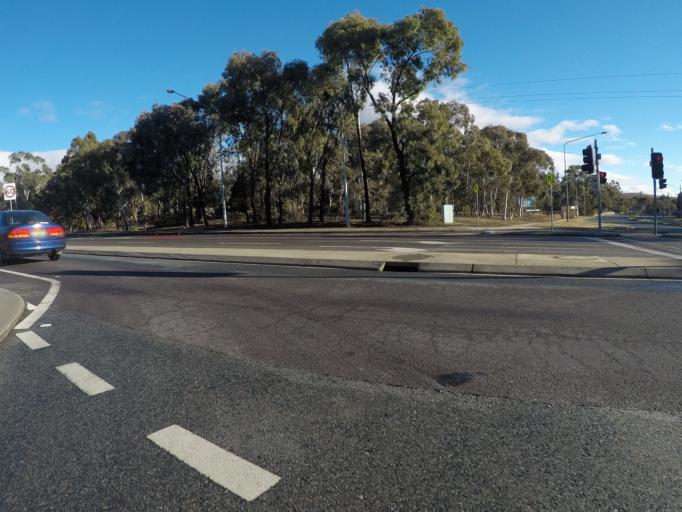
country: AU
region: Australian Capital Territory
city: Belconnen
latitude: -35.2422
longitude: 149.0901
